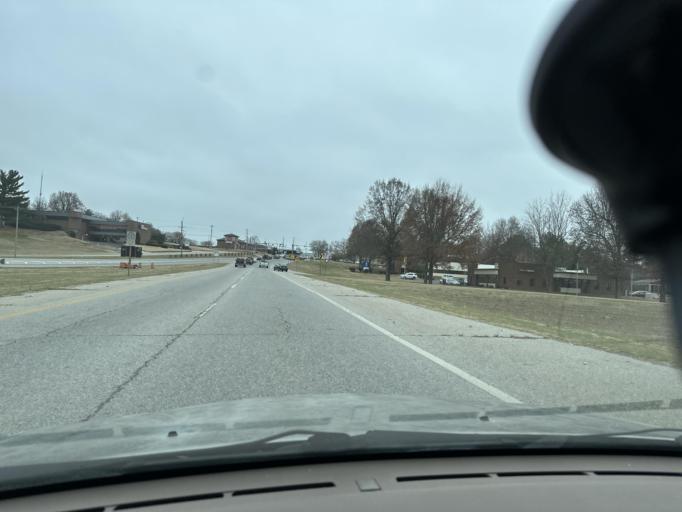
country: US
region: Arkansas
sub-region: Washington County
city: Johnson
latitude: 36.1168
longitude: -94.1456
